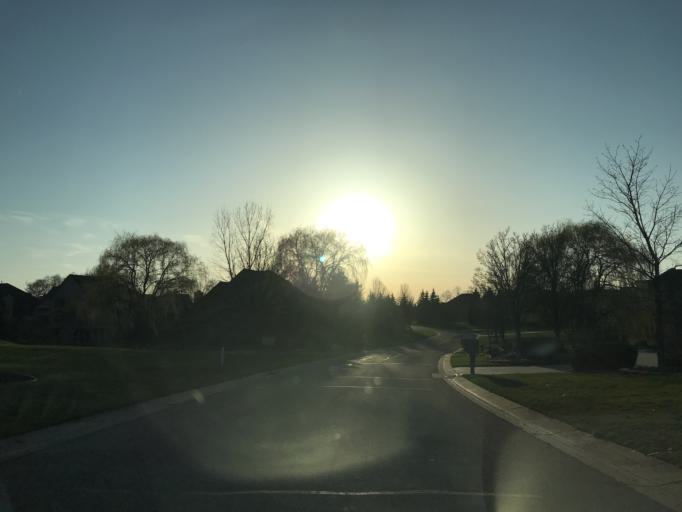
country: US
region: Michigan
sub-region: Oakland County
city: South Lyon
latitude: 42.4586
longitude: -83.5863
